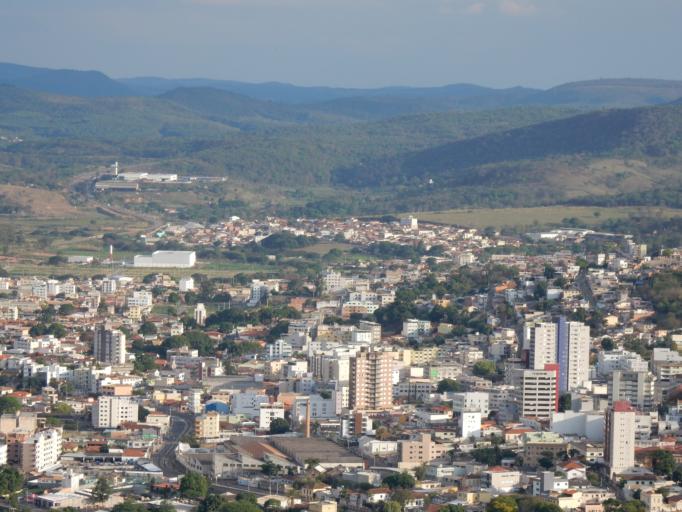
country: BR
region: Minas Gerais
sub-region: Itauna
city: Itauna
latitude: -20.0563
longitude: -44.5820
